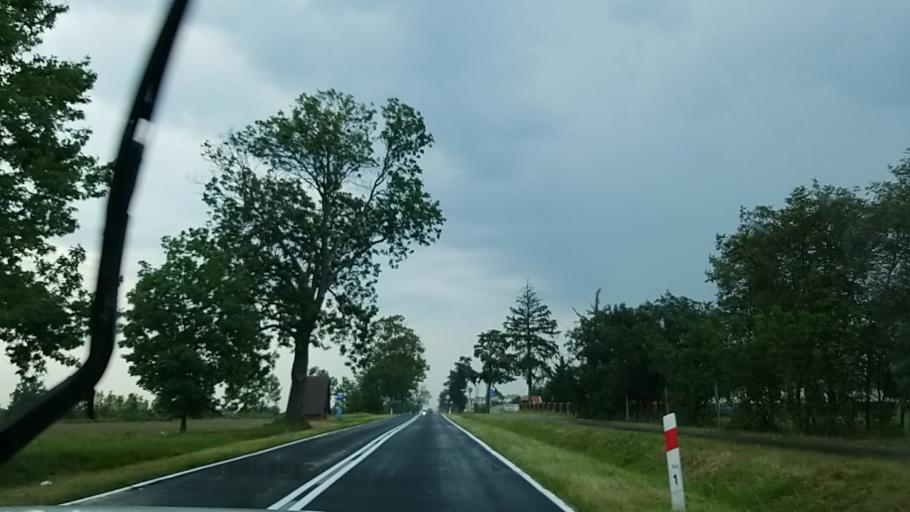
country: PL
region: Lublin Voivodeship
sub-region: Powiat wlodawski
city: Wlodawa
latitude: 51.6106
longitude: 23.5298
